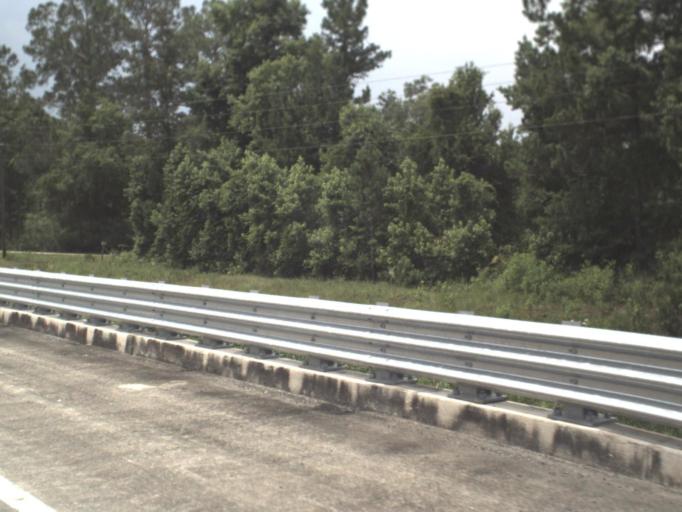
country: US
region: Florida
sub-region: Levy County
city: Chiefland
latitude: 29.3320
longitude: -82.7715
